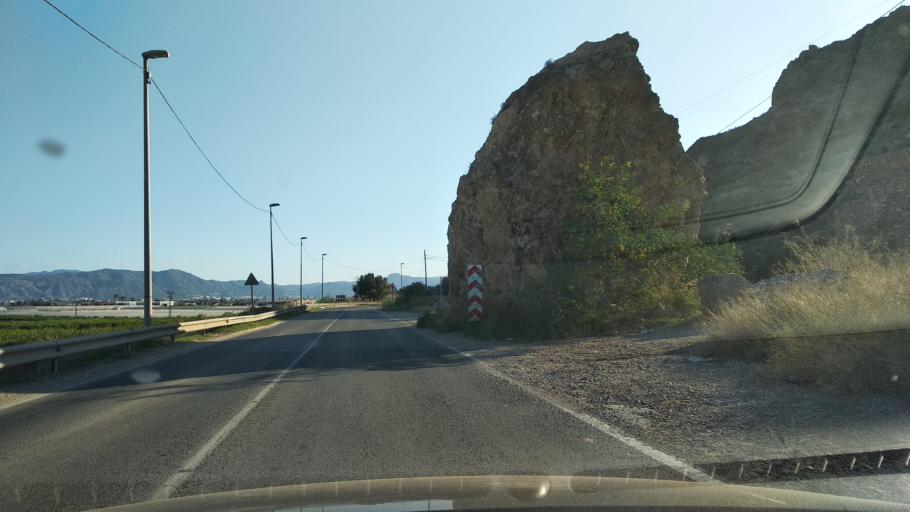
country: ES
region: Murcia
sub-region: Murcia
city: Santomera
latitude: 38.0555
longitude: -1.0525
